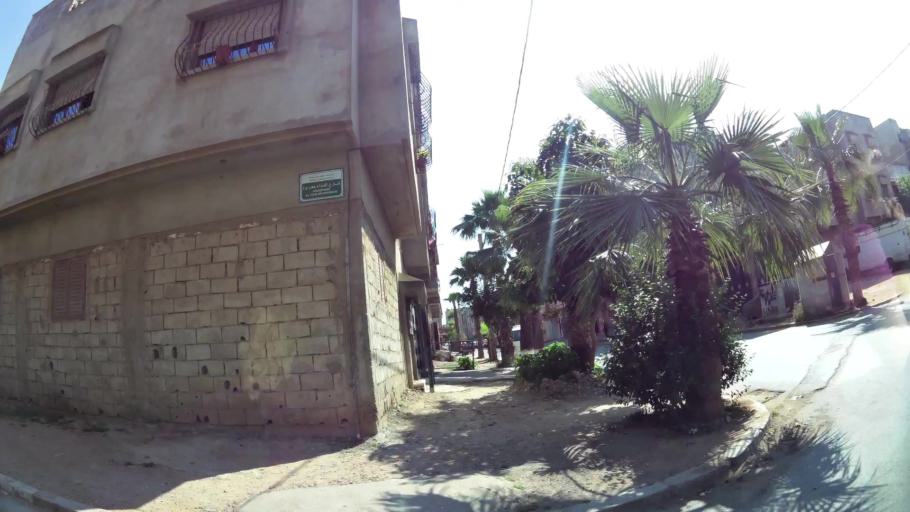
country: MA
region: Rabat-Sale-Zemmour-Zaer
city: Sale
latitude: 34.0692
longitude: -6.7733
